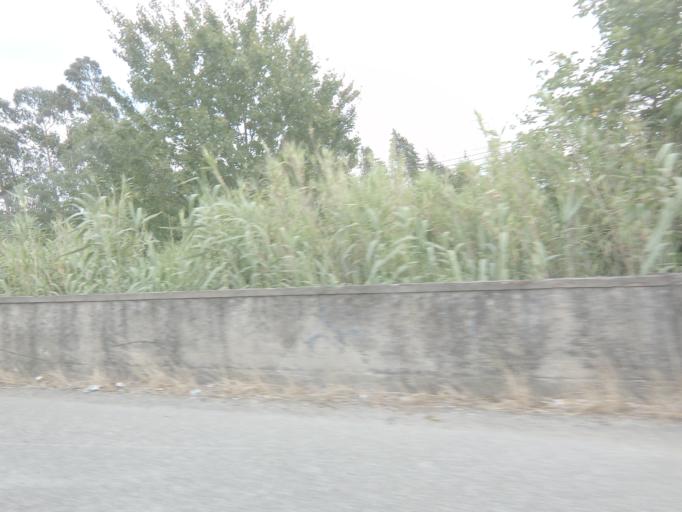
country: PT
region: Coimbra
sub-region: Condeixa-A-Nova
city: Condeixa-a-Nova
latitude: 40.1378
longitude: -8.4684
